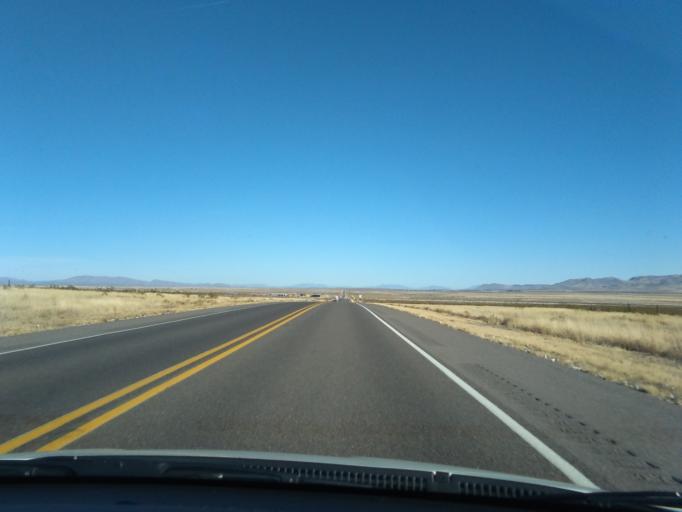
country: US
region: New Mexico
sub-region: Dona Ana County
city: Hatch
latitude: 32.5769
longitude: -107.3940
